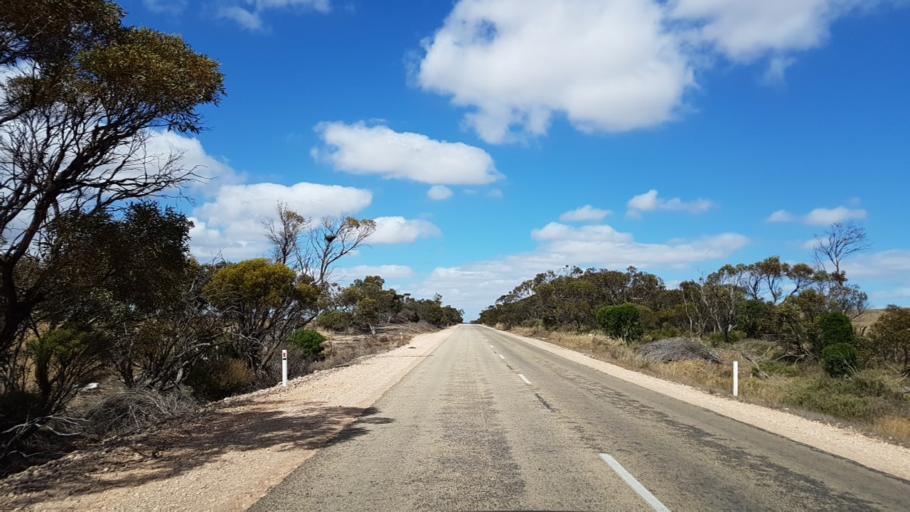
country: AU
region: South Australia
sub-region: Yorke Peninsula
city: Ardrossan
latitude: -34.5440
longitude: 137.8541
